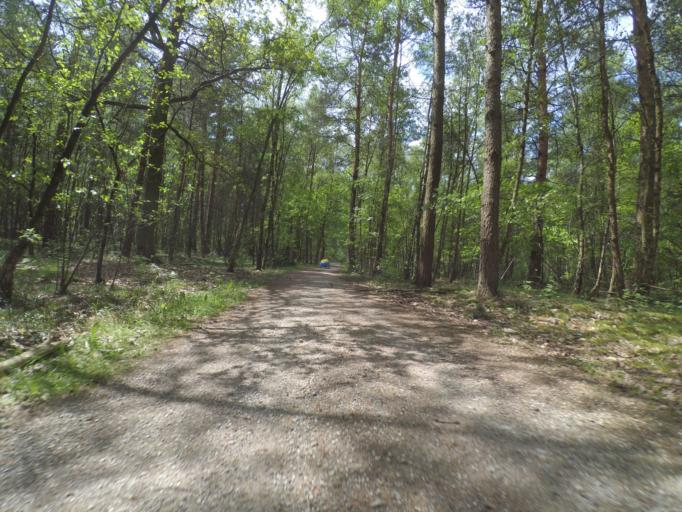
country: DE
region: Lower Saxony
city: Wietze
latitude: 52.6681
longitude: 9.8220
